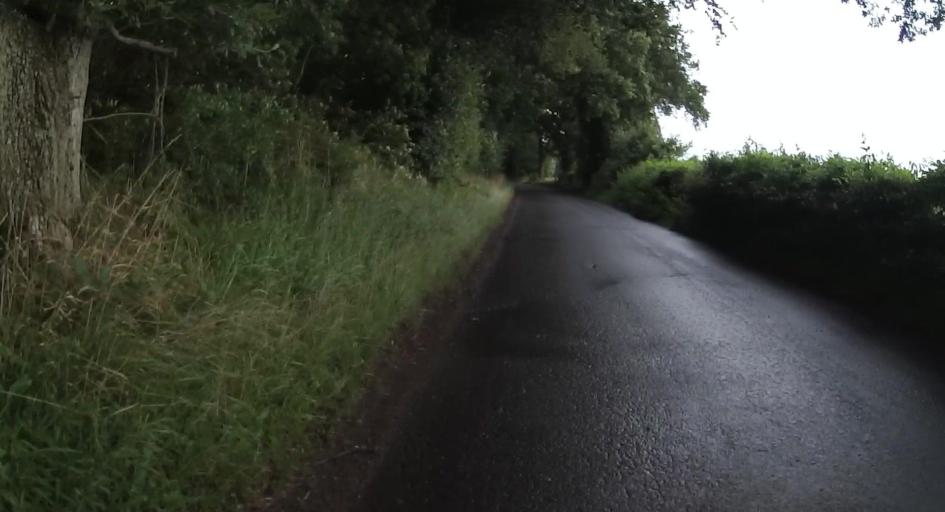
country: GB
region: England
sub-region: Hampshire
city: Andover
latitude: 51.2000
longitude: -1.4105
